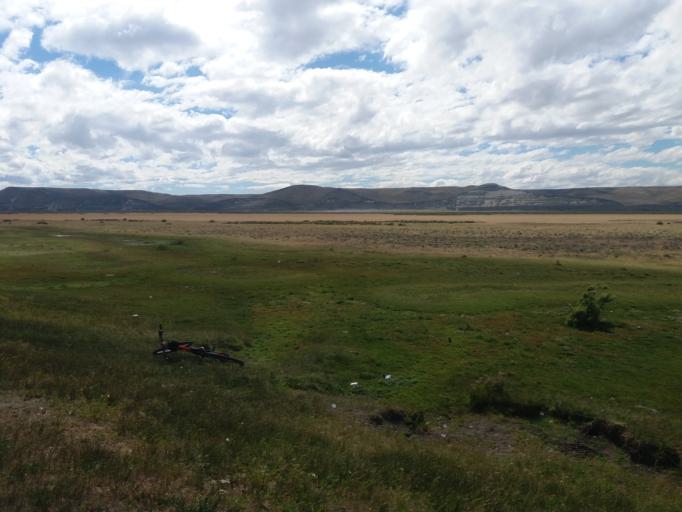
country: AR
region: Santa Cruz
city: Rio Gallegos
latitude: -51.6259
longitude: -69.5324
